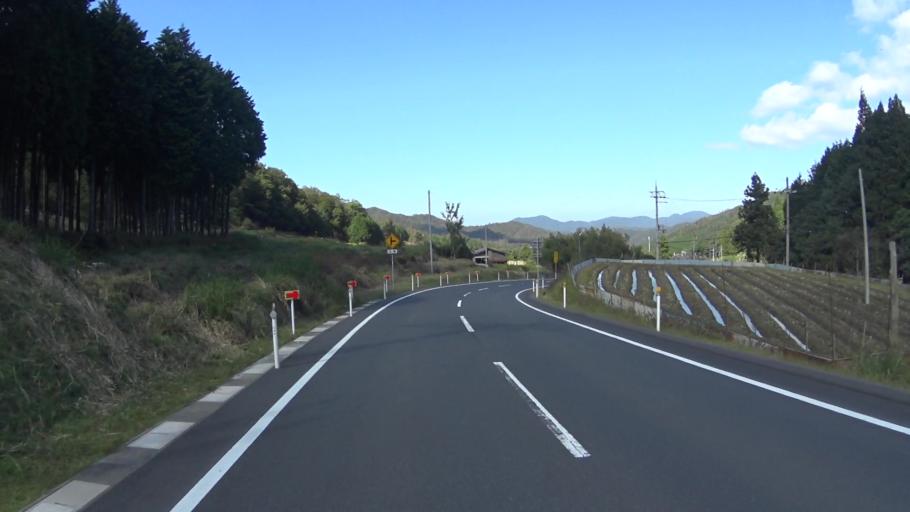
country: JP
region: Hyogo
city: Toyooka
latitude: 35.5398
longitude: 134.9785
